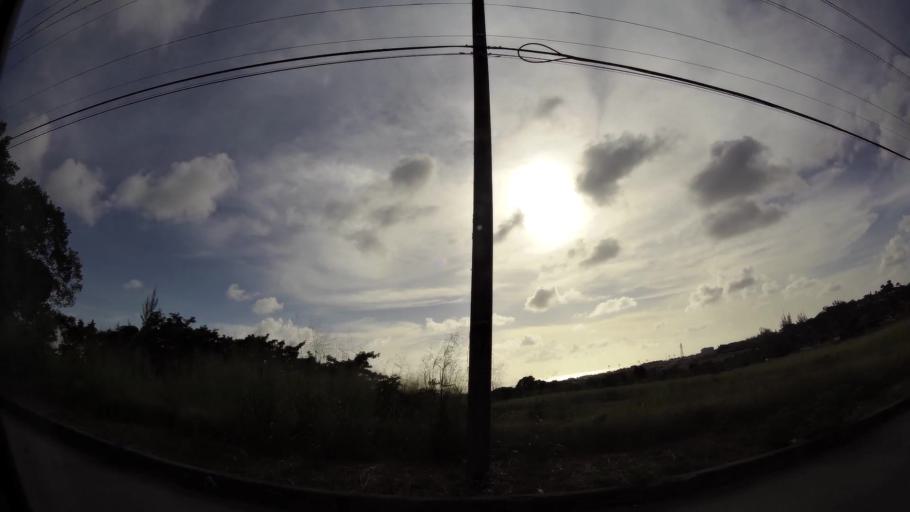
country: BB
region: Christ Church
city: Oistins
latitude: 13.0934
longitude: -59.5681
